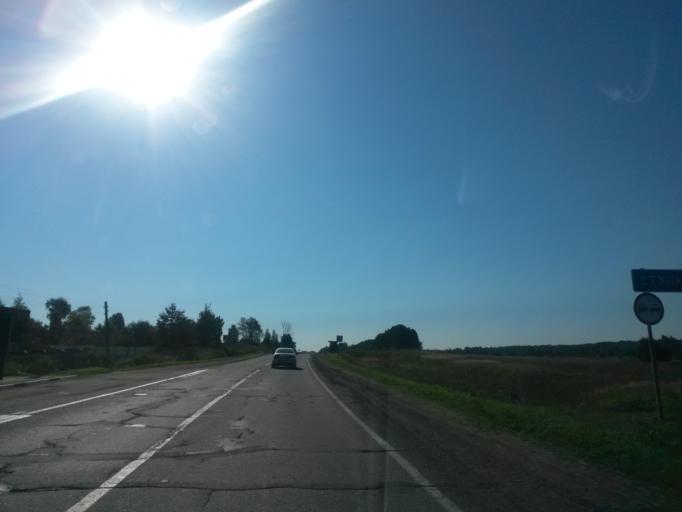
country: RU
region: Jaroslavl
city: Krasnyye Tkachi
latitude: 57.3963
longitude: 39.6738
